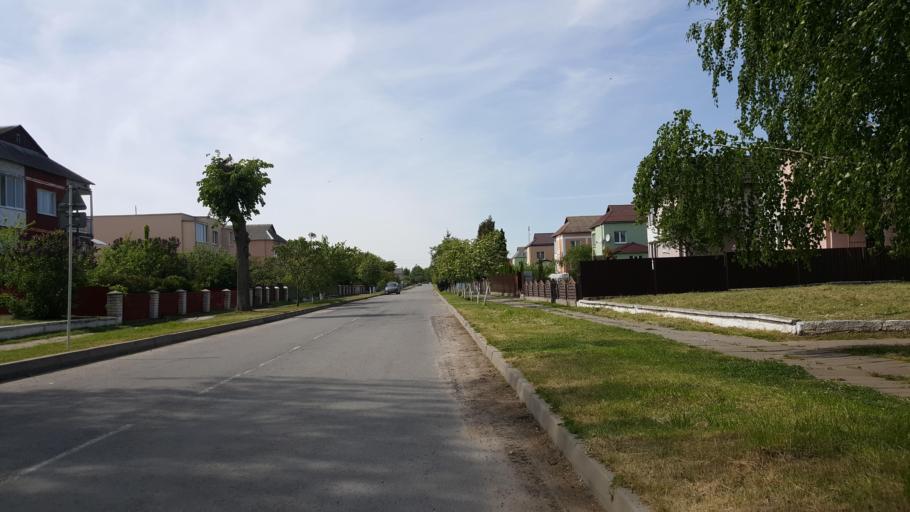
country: BY
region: Brest
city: Charnawchytsy
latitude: 52.2632
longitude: 23.5933
